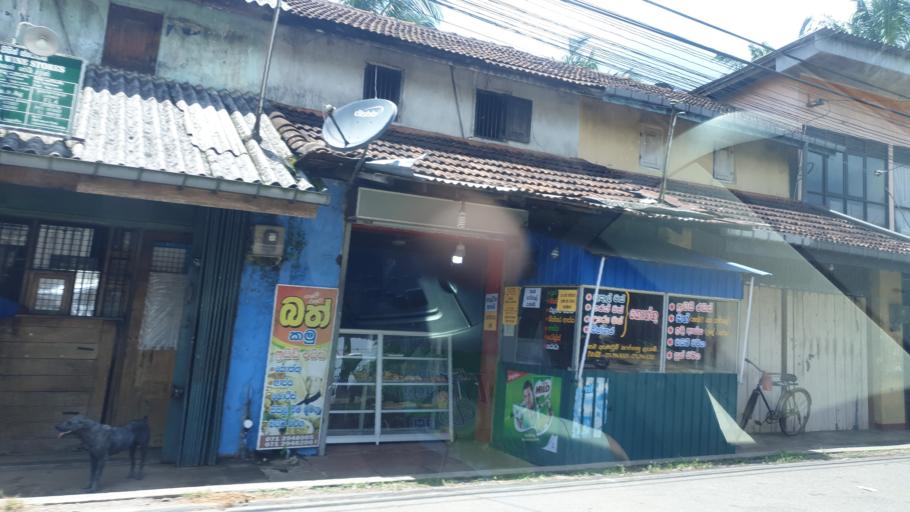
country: LK
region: Western
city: Horawala Junction
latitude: 6.5247
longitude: 80.2141
